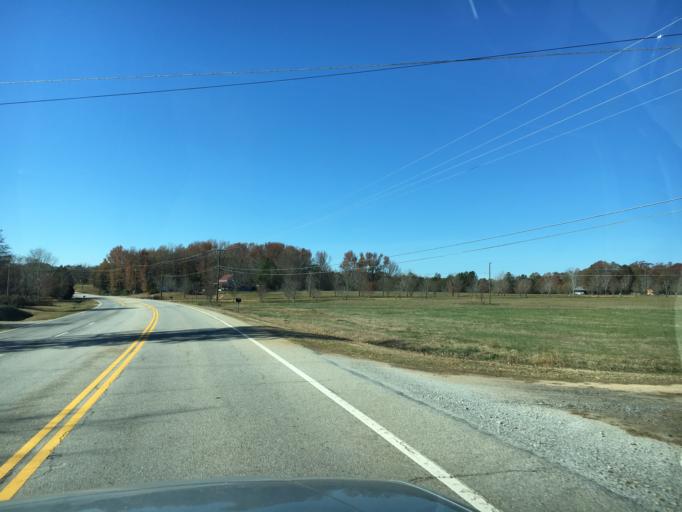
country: US
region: Georgia
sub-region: Hart County
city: Hartwell
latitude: 34.3479
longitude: -82.8770
